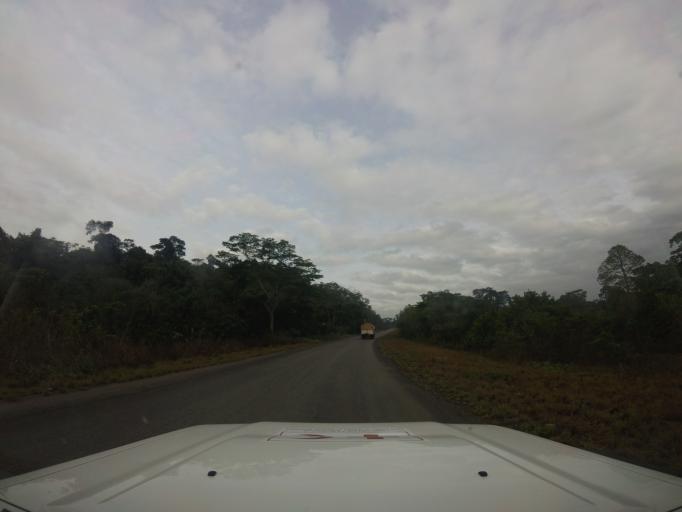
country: LR
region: Bomi
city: Tubmanburg
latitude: 6.7175
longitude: -11.0700
